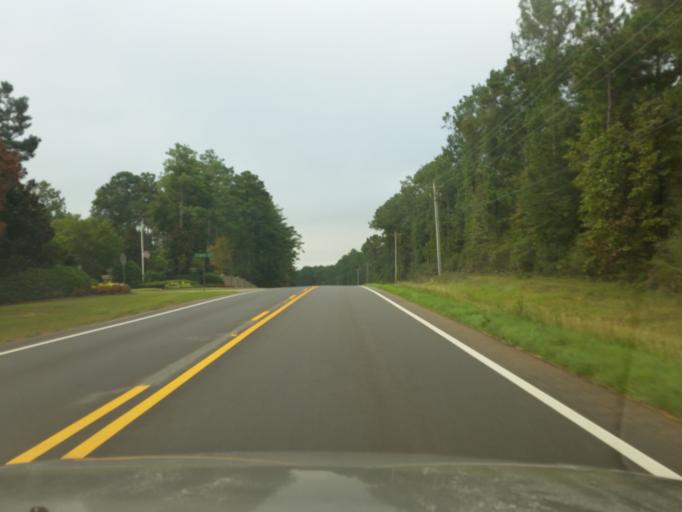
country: US
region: Alabama
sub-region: Baldwin County
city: Spanish Fort
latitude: 30.7177
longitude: -87.9015
